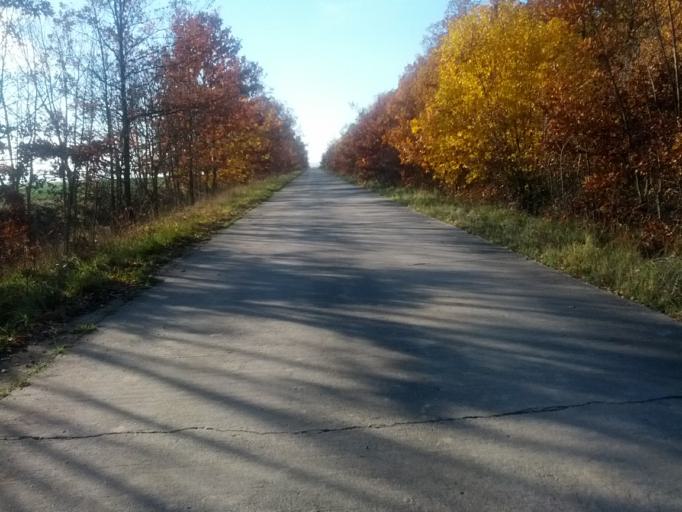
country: DE
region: Thuringia
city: Mechterstadt
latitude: 50.9603
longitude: 10.5480
